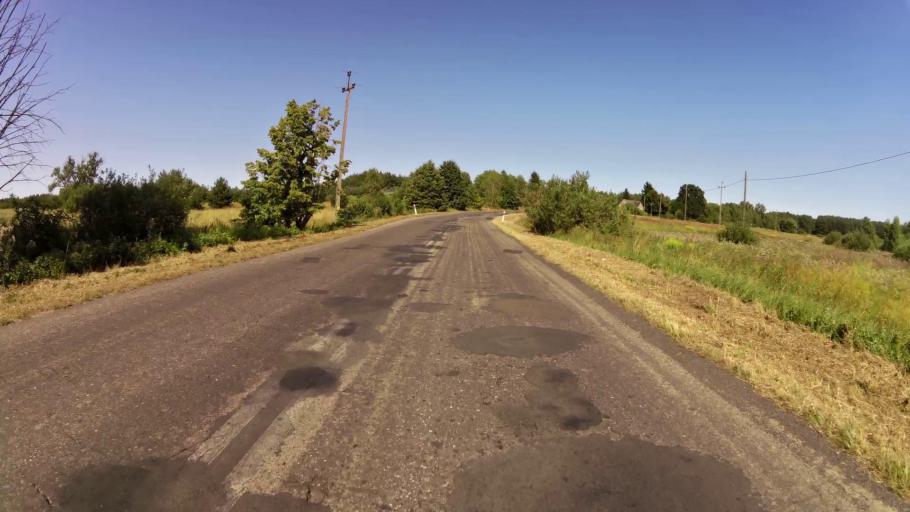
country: PL
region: West Pomeranian Voivodeship
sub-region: Powiat stargardzki
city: Dobrzany
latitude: 53.3473
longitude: 15.3943
